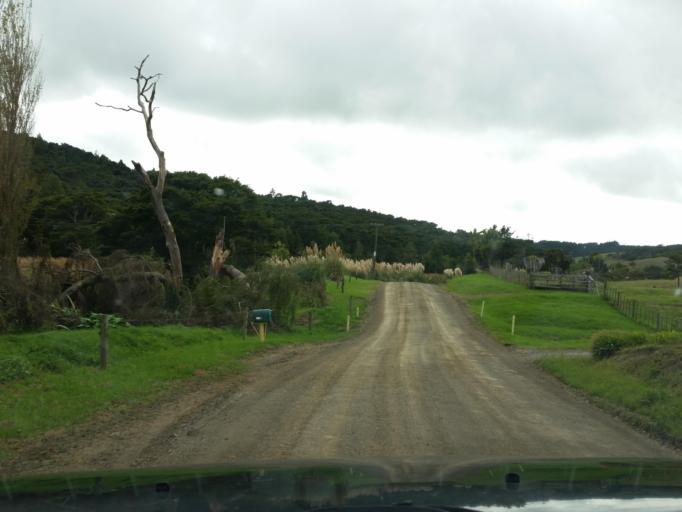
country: NZ
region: Northland
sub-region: Kaipara District
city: Dargaville
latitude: -36.1204
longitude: 174.1273
